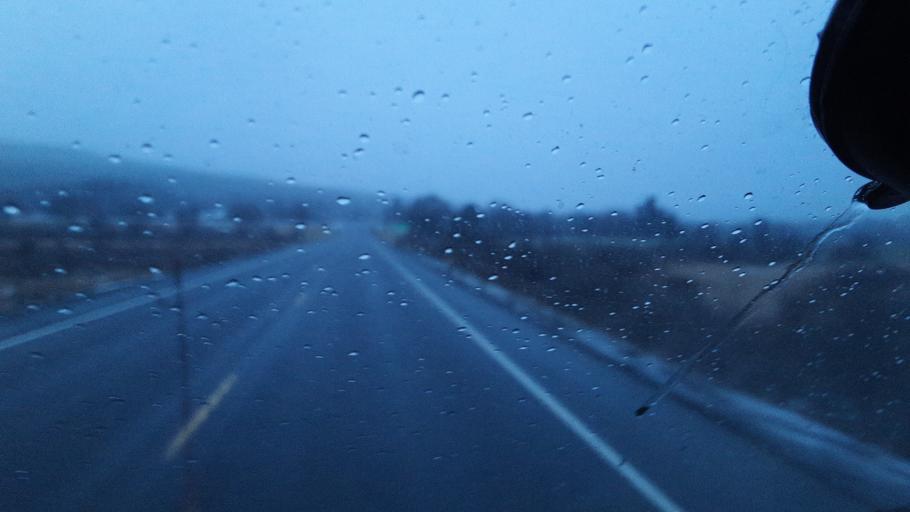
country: US
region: New York
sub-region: Allegany County
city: Belmont
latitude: 42.2559
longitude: -78.0603
